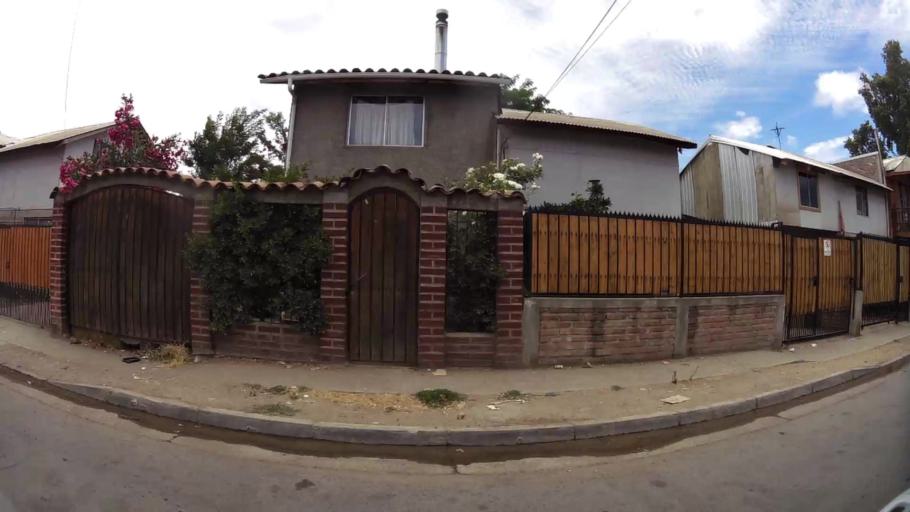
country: CL
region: O'Higgins
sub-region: Provincia de Cachapoal
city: Graneros
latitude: -34.0682
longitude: -70.7352
